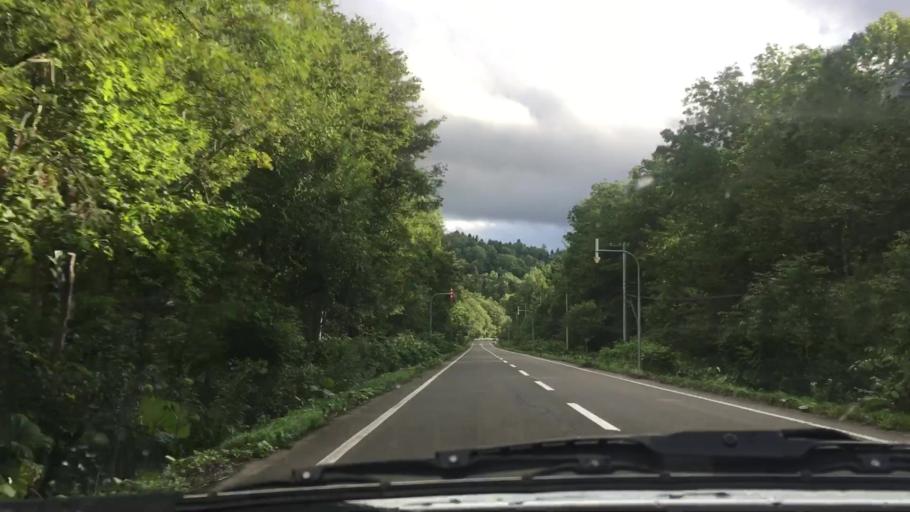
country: JP
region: Hokkaido
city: Shimo-furano
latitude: 43.0896
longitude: 142.6811
